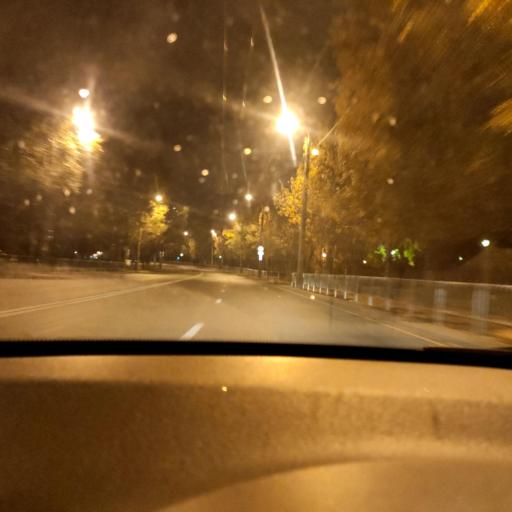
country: RU
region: Samara
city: Samara
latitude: 53.2426
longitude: 50.2287
